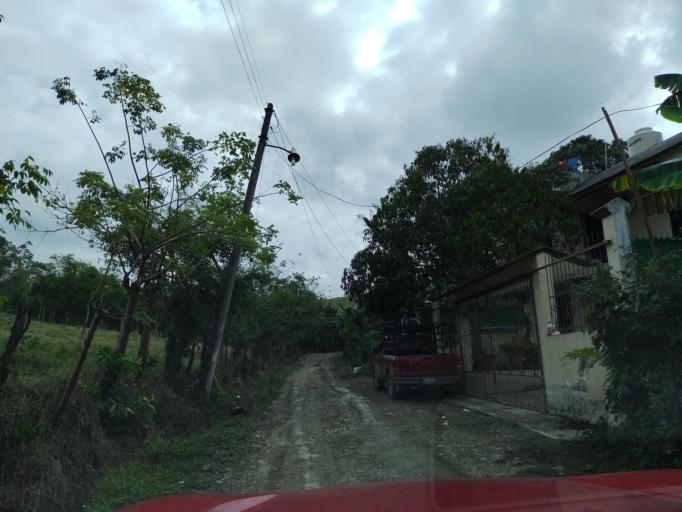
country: MX
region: Veracruz
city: Coatzintla
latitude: 20.4565
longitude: -97.4193
